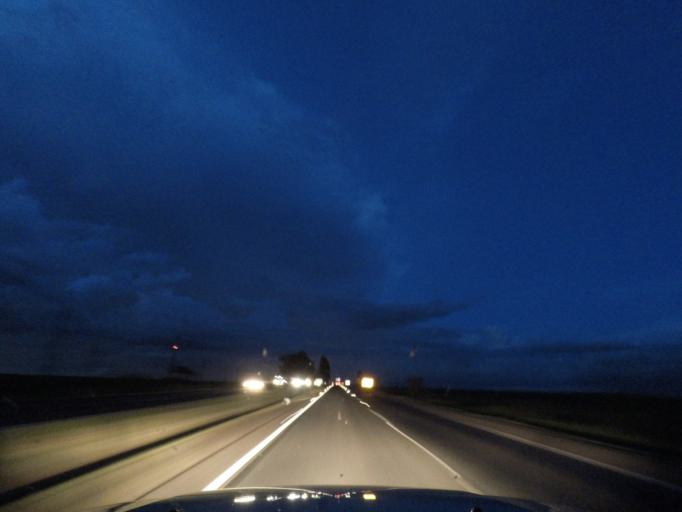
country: BR
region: Minas Gerais
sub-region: Uberlandia
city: Uberlandia
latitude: -19.1954
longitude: -48.1531
